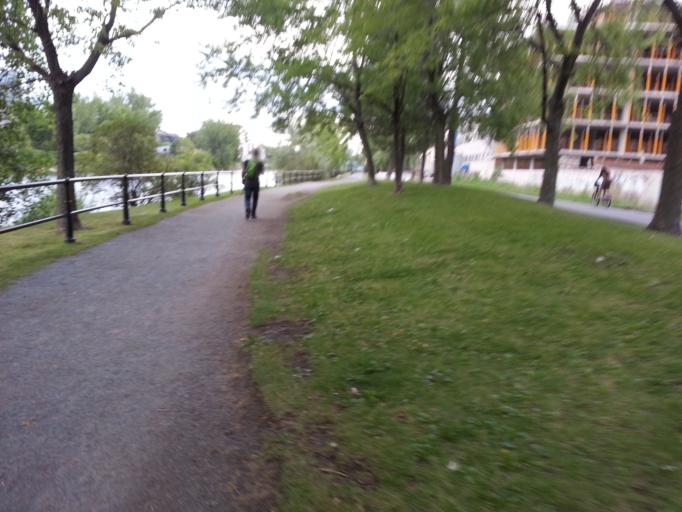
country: CA
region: Quebec
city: Westmount
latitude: 45.4823
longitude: -73.5694
